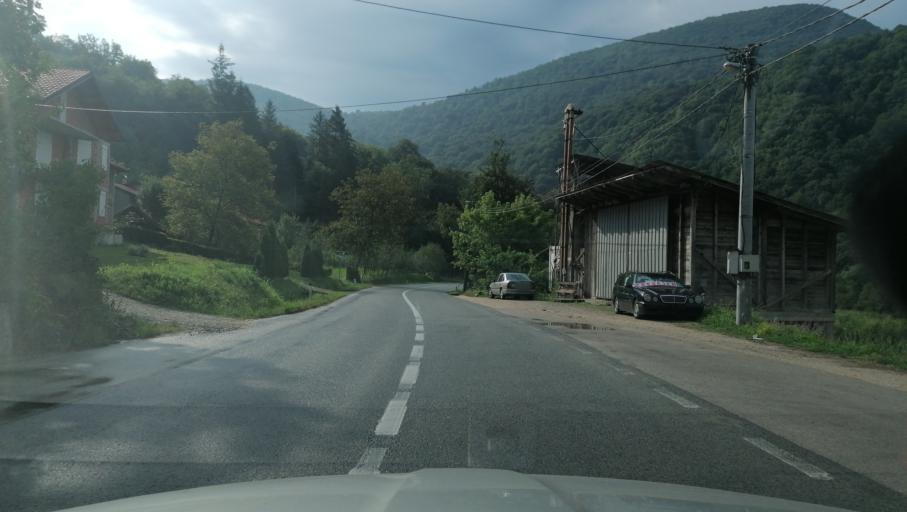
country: BA
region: Republika Srpska
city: Hiseti
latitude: 44.6736
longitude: 17.1544
